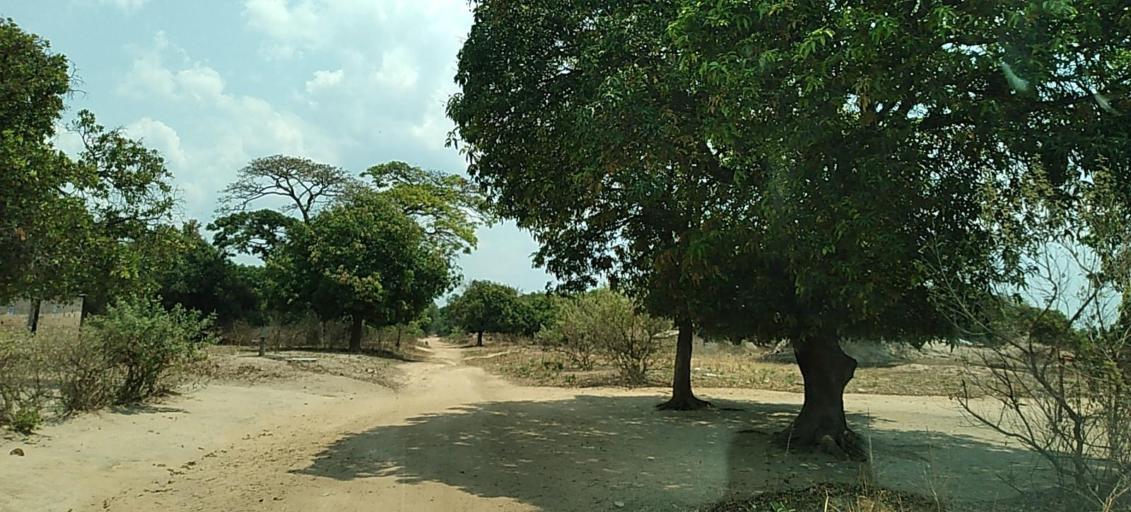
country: ZM
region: Copperbelt
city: Luanshya
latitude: -13.1632
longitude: 28.3066
